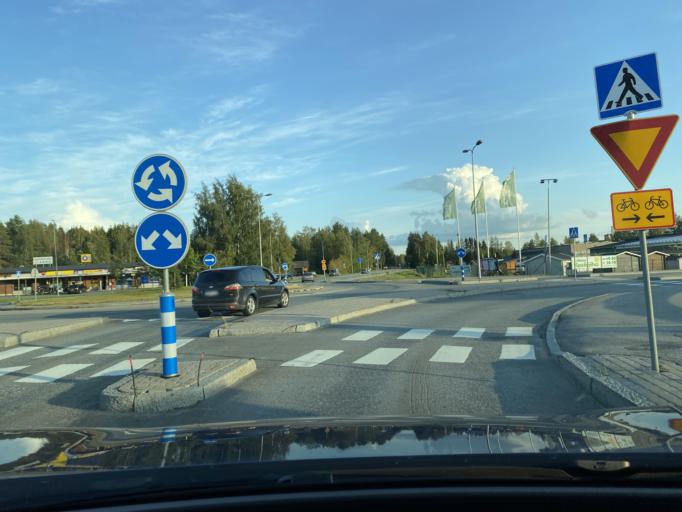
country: FI
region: Southern Ostrobothnia
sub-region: Seinaejoki
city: Nurmo
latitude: 62.8057
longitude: 22.8798
